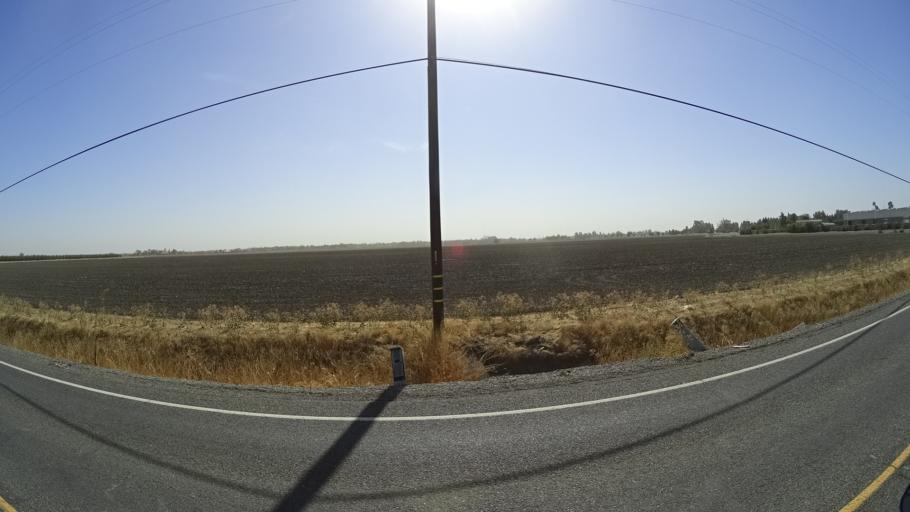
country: US
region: California
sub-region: Yolo County
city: Davis
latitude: 38.5903
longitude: -121.7617
